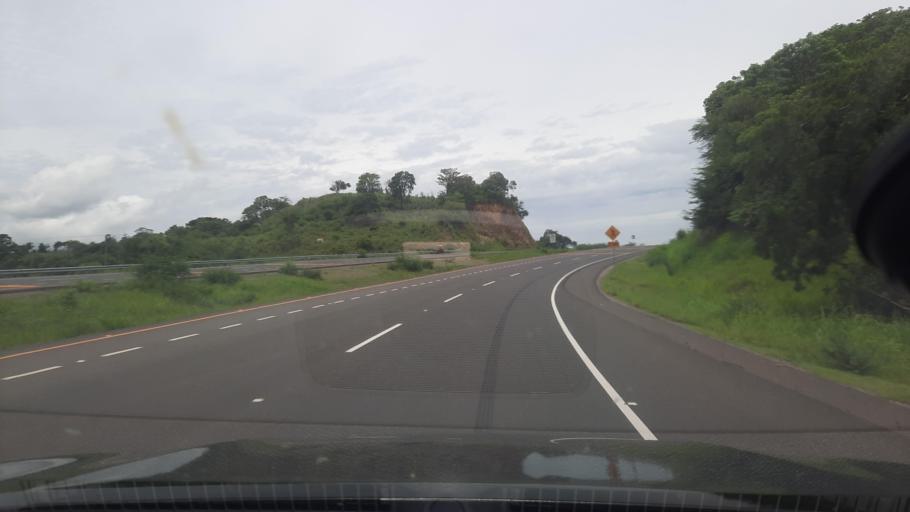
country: HN
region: Valle
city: Aramecina
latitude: 13.7492
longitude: -87.7158
